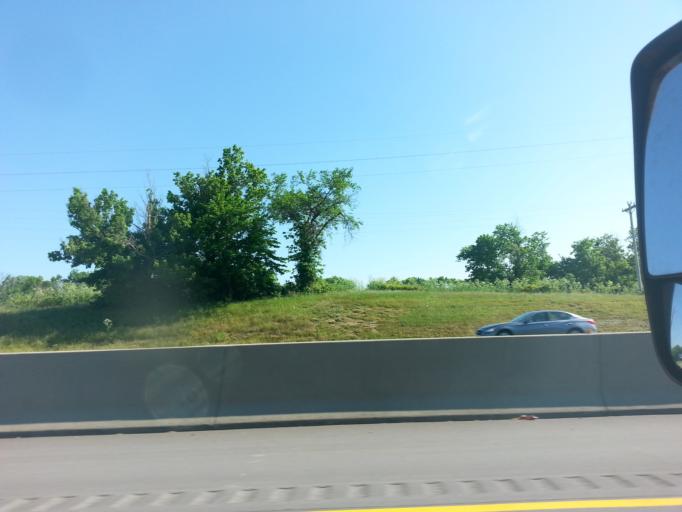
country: US
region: Kentucky
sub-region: Shelby County
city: Simpsonville
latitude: 38.2043
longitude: -85.3265
